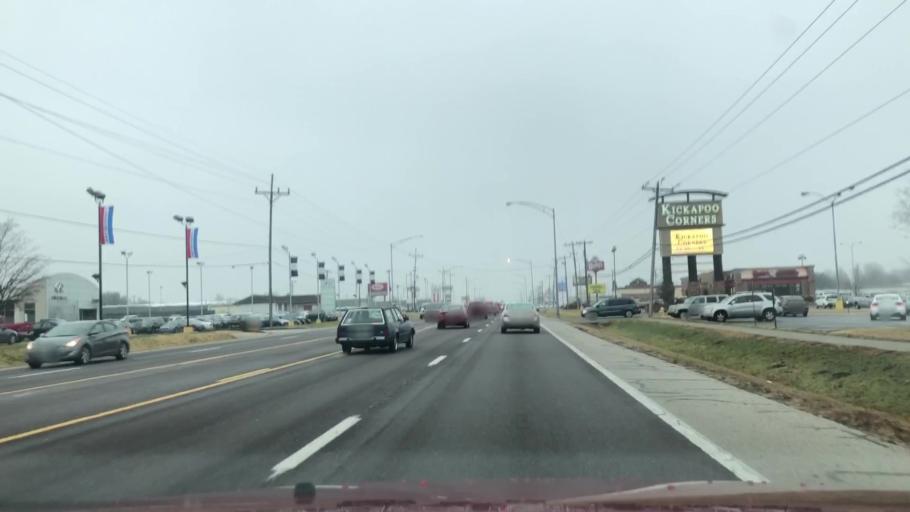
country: US
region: Missouri
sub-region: Greene County
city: Springfield
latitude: 37.1477
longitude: -93.2958
